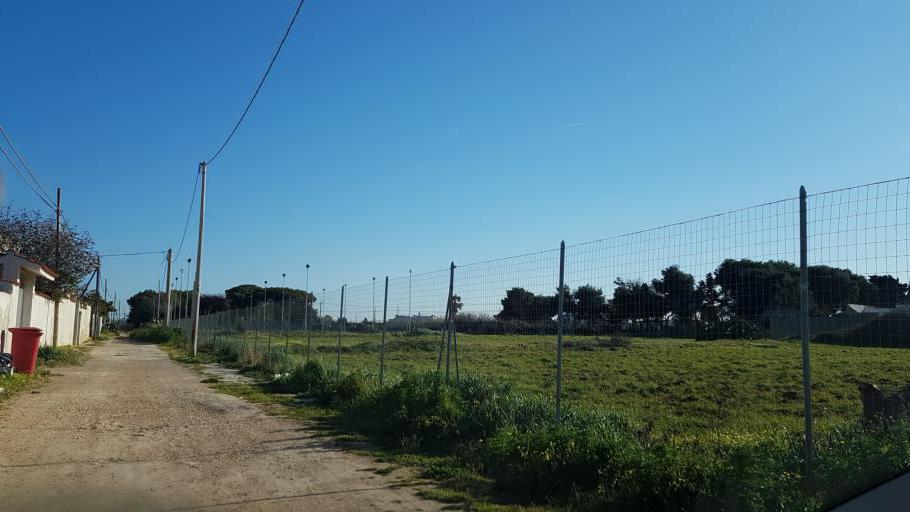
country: IT
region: Apulia
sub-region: Provincia di Brindisi
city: Materdomini
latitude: 40.6708
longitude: 17.9438
